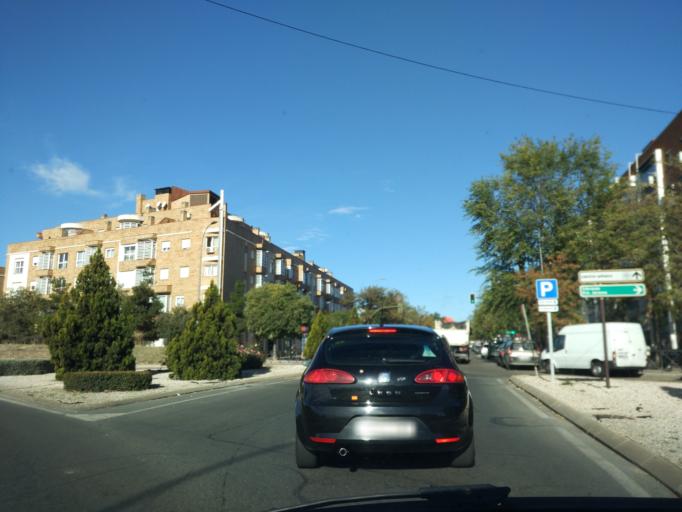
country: ES
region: Madrid
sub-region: Provincia de Madrid
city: Torrejon de Ardoz
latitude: 40.4489
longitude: -3.4691
